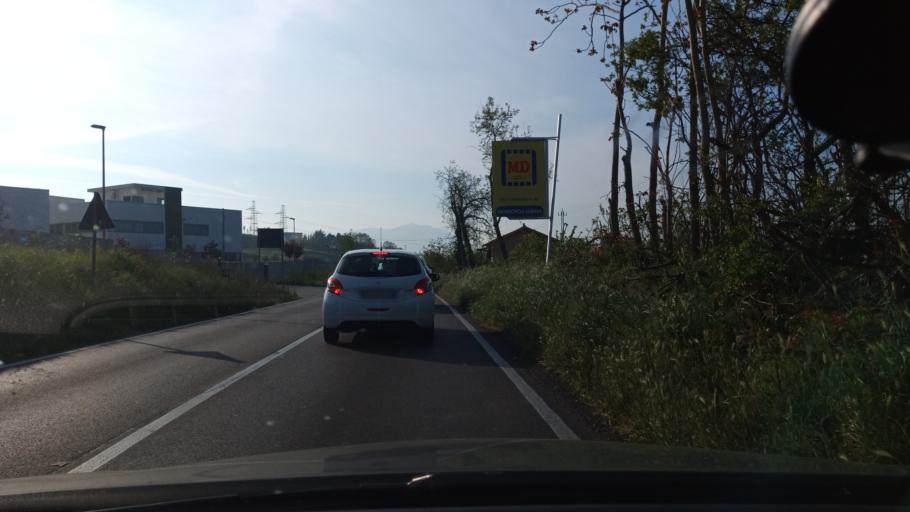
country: IT
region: Latium
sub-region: Citta metropolitana di Roma Capitale
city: Fiano Romano
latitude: 42.1678
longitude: 12.6393
